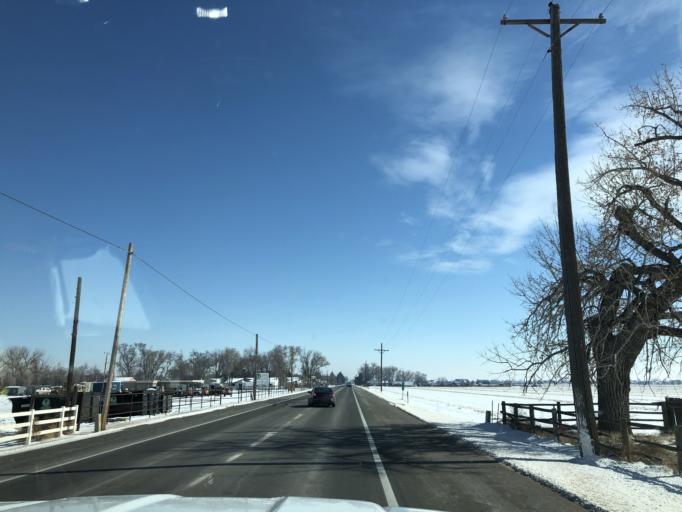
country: US
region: Colorado
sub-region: Morgan County
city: Fort Morgan
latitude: 40.2541
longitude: -103.8587
